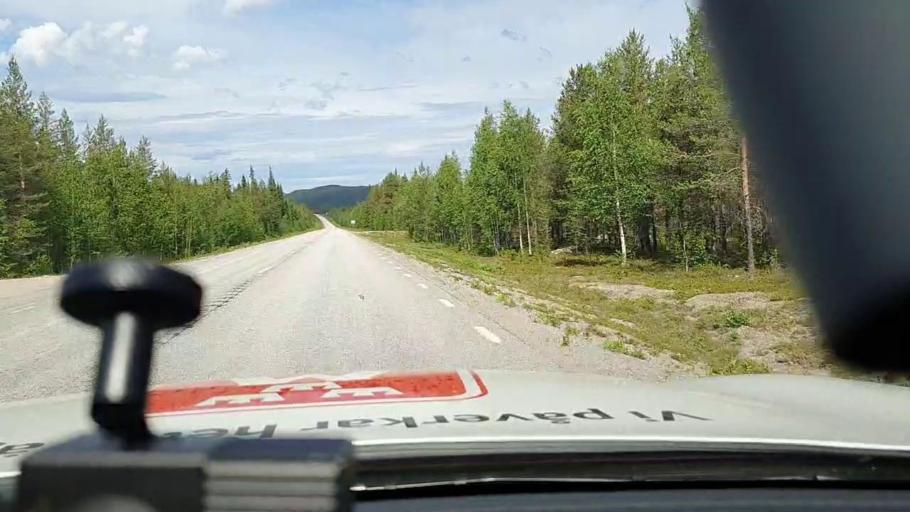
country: SE
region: Norrbotten
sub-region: Jokkmokks Kommun
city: Jokkmokk
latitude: 66.5445
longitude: 20.1370
